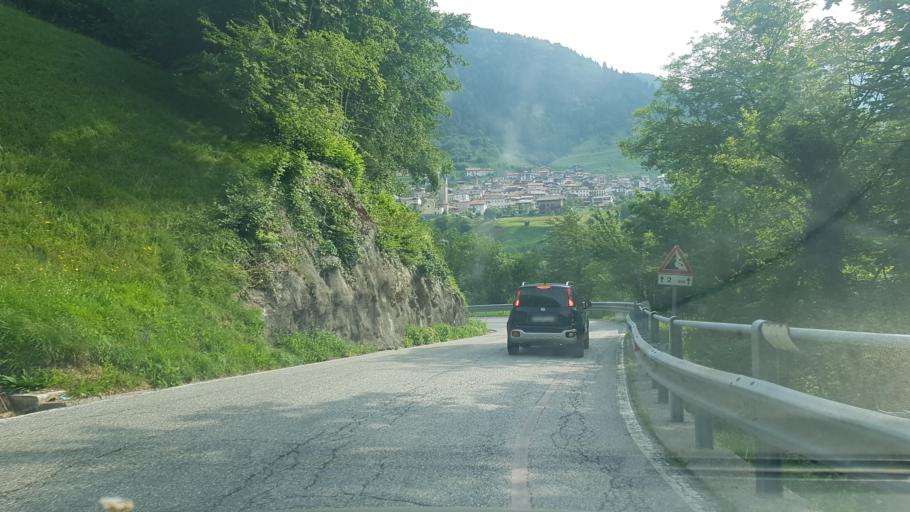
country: IT
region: Friuli Venezia Giulia
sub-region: Provincia di Udine
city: Paularo
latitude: 46.5119
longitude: 13.1233
